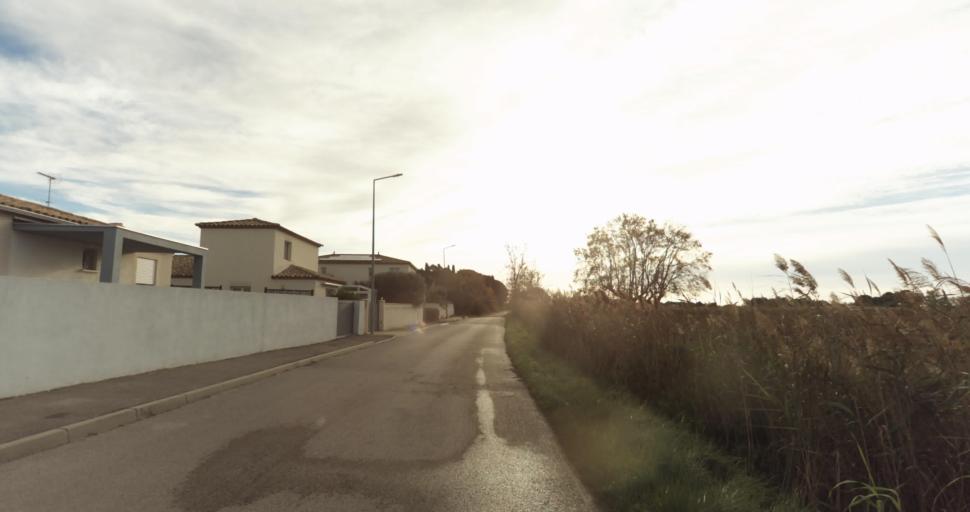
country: FR
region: Languedoc-Roussillon
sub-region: Departement du Gard
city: Aigues-Mortes
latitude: 43.5610
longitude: 4.2052
